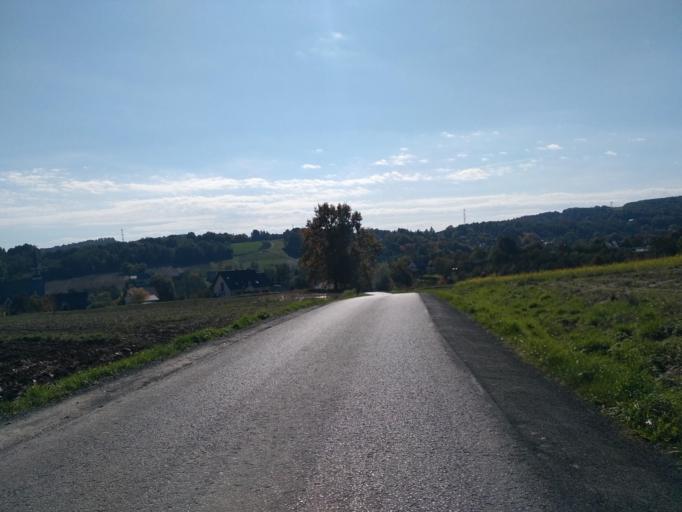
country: PL
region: Subcarpathian Voivodeship
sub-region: Powiat debicki
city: Slotowa
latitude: 49.9490
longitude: 21.2906
